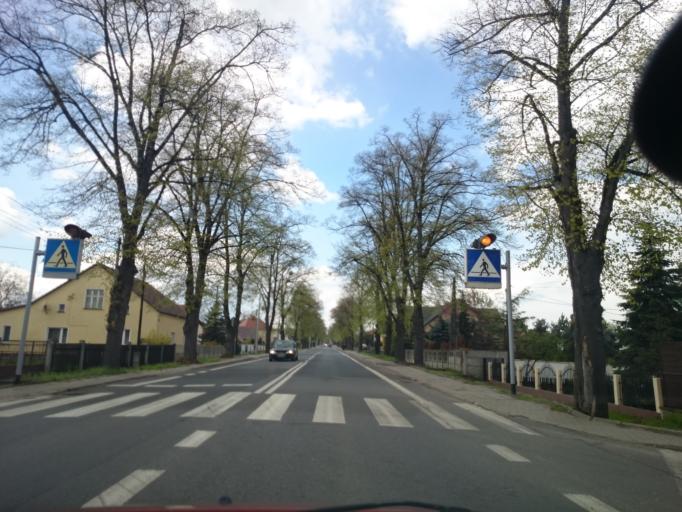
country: PL
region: Opole Voivodeship
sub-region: Powiat opolski
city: Opole
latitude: 50.6452
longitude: 17.9860
